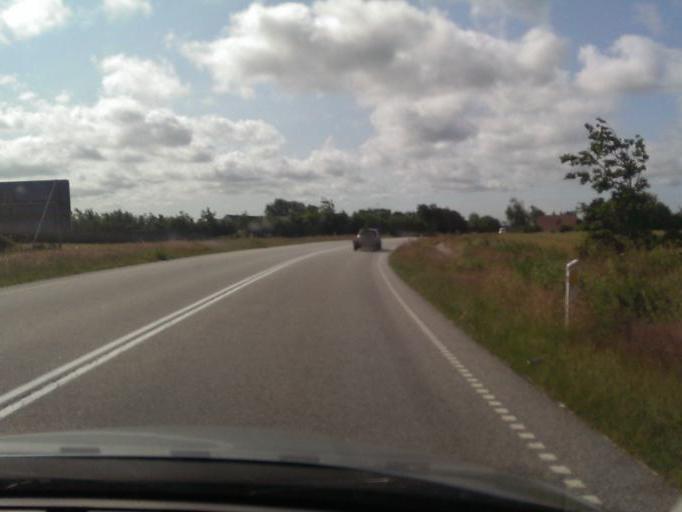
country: DK
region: North Denmark
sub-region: Bronderslev Kommune
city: Bronderslev
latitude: 57.2509
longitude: 9.9670
